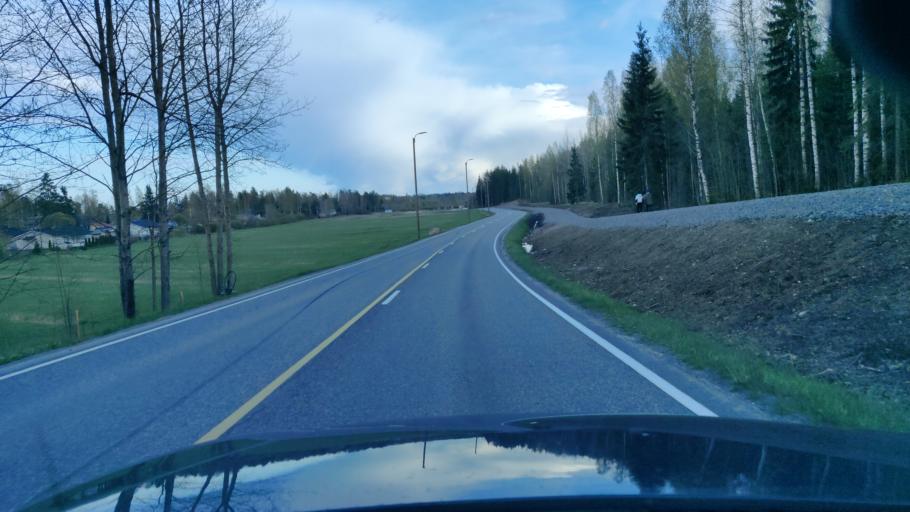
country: FI
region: Uusimaa
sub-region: Helsinki
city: Jaervenpaeae
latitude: 60.4762
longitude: 25.0657
